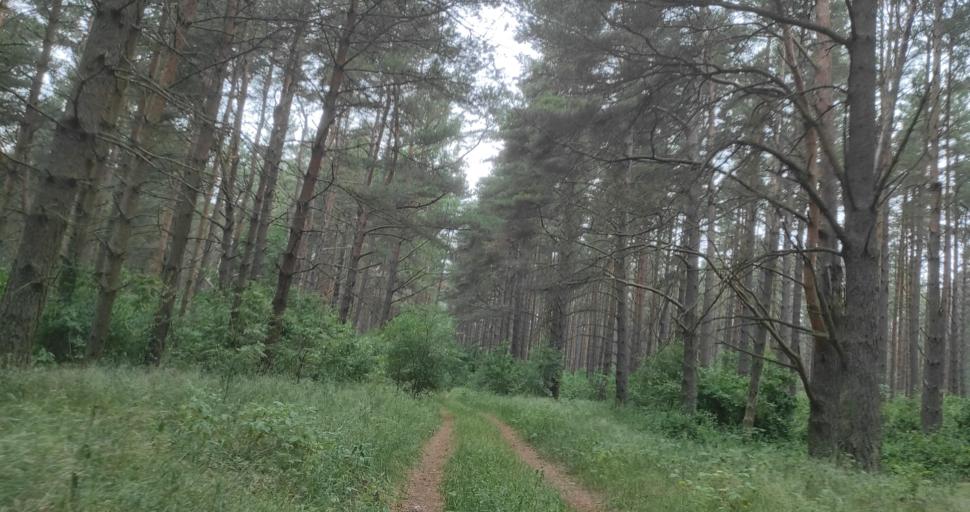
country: LV
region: Pavilostas
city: Pavilosta
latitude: 56.8864
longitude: 21.1996
